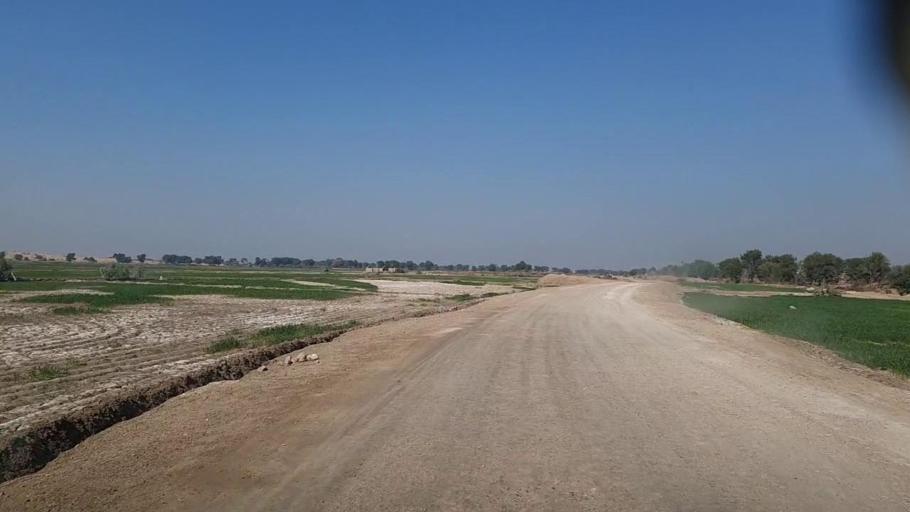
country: PK
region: Sindh
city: Khairpur
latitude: 27.9839
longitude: 69.8494
